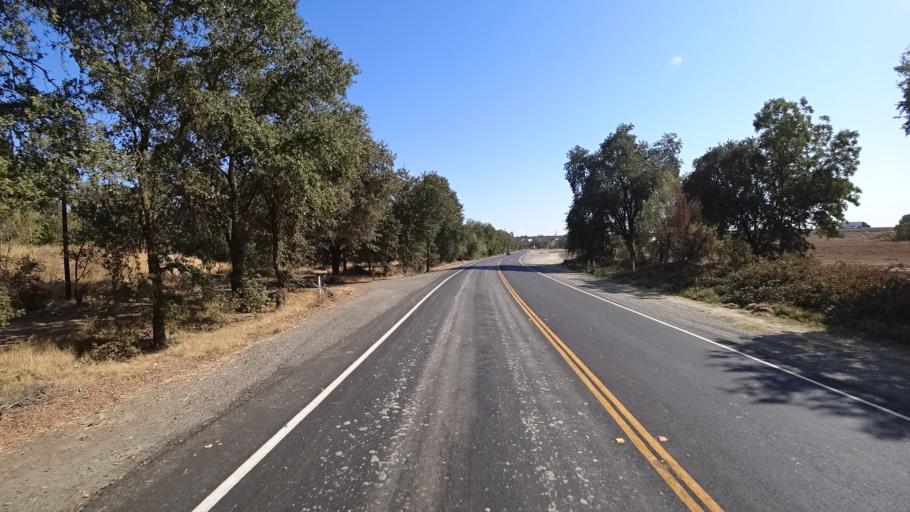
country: US
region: California
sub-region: Yolo County
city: Woodland
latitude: 38.6762
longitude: -121.6352
